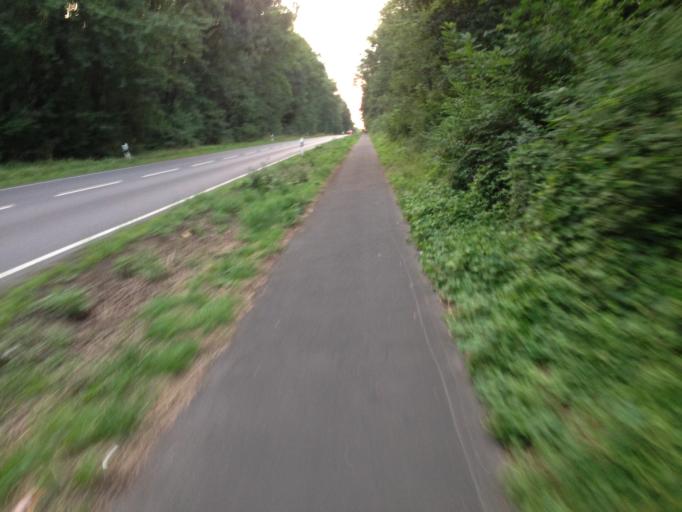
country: DE
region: Hesse
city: Allendorf an der Lahn
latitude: 50.5454
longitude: 8.6489
